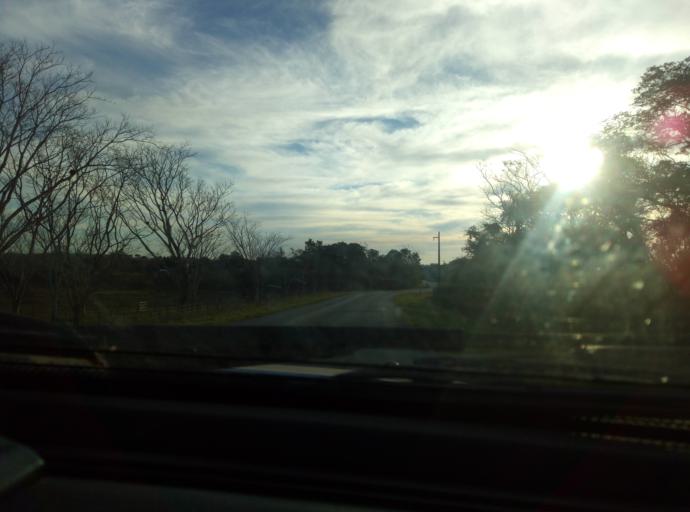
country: PY
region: Caaguazu
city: Carayao
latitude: -25.1523
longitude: -56.3300
